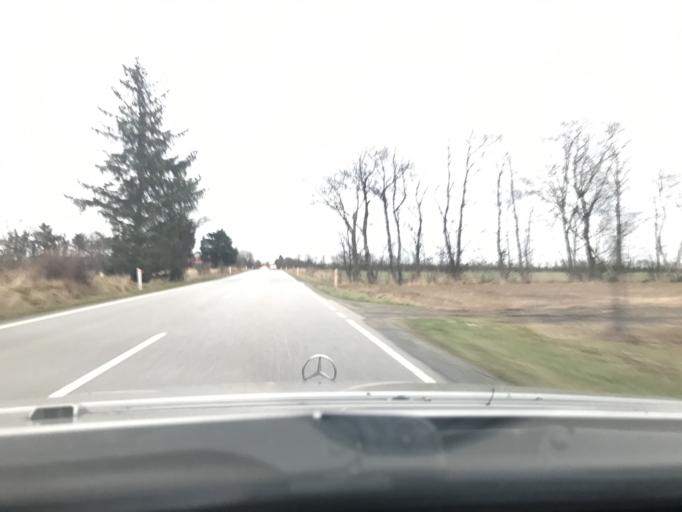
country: DK
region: South Denmark
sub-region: Aabenraa Kommune
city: Rodekro
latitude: 55.0755
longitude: 9.2419
